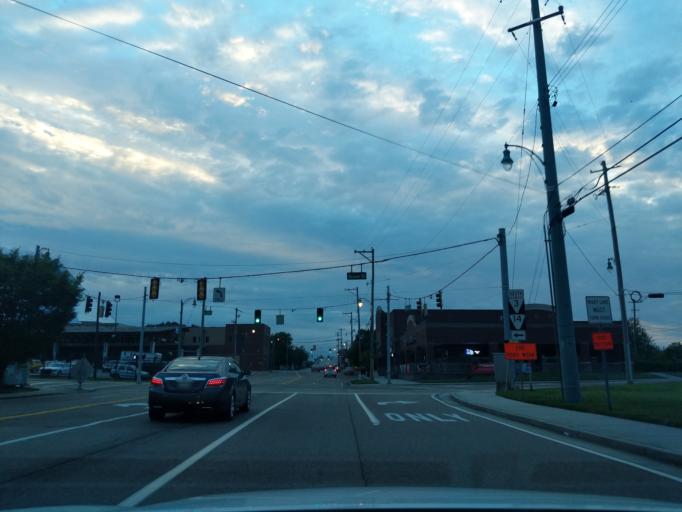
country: US
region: Tennessee
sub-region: Shelby County
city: Memphis
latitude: 35.1572
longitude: -90.0473
